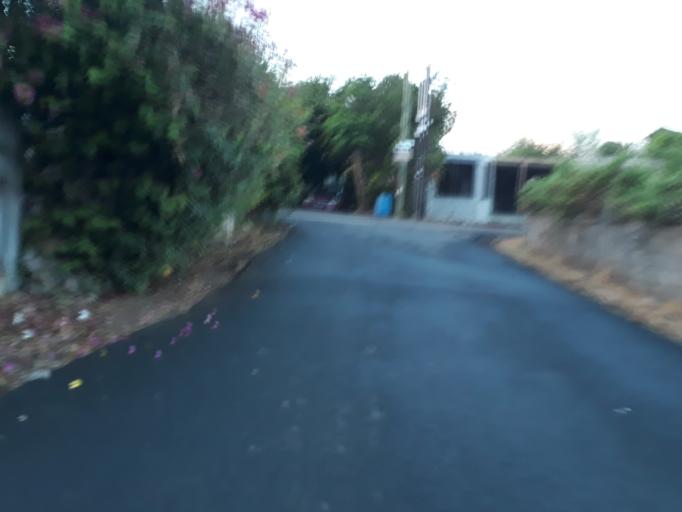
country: MU
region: Riviere du Rempart
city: Grand Baie
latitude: -20.0163
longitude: 57.5826
